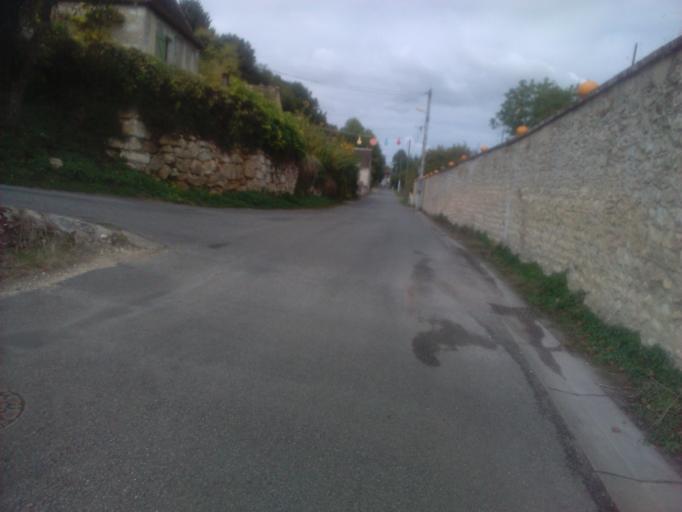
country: FR
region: Centre
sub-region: Departement du Loir-et-Cher
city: Villiers-sur-Loir
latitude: 47.7988
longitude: 0.9809
